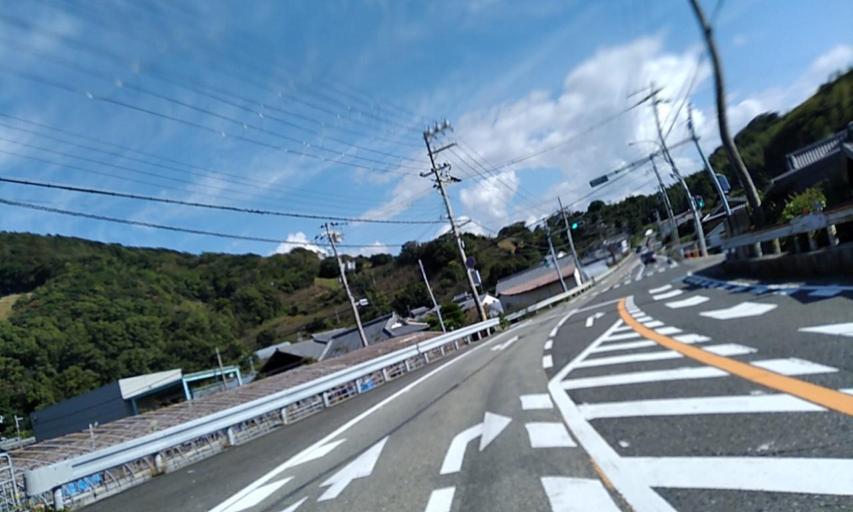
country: JP
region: Wakayama
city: Tanabe
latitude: 33.7832
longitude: 135.2856
